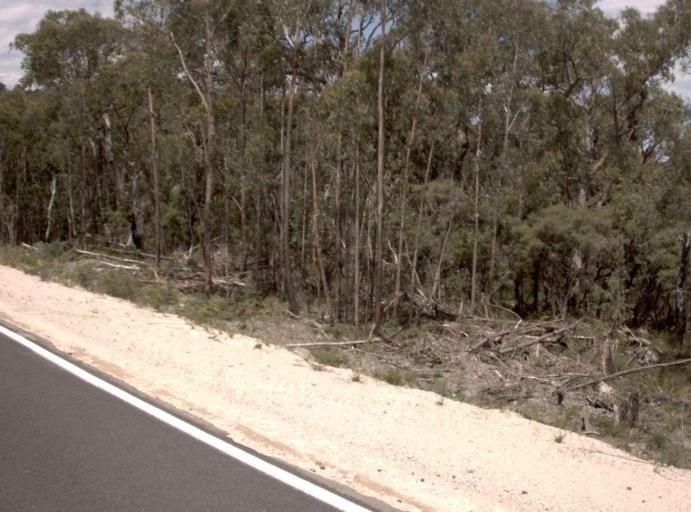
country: AU
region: New South Wales
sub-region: Bombala
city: Bombala
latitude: -37.5654
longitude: 149.2348
